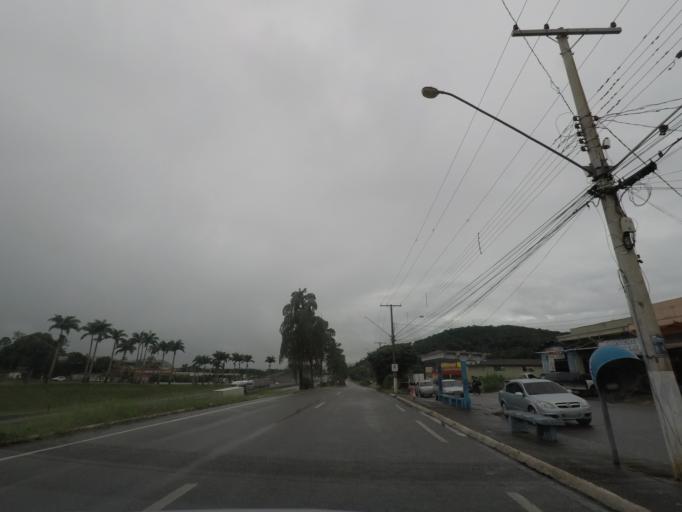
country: BR
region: Sao Paulo
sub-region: Jacupiranga
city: Jacupiranga
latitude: -24.6978
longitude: -48.0016
